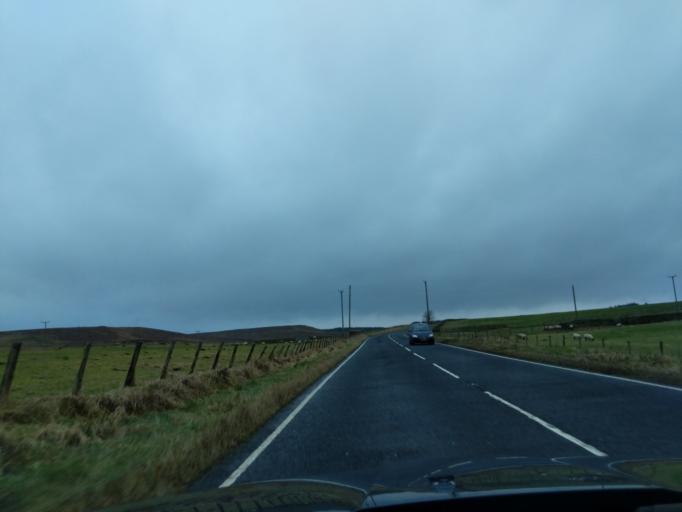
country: GB
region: England
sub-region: Northumberland
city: Corsenside
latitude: 55.1919
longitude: -2.0657
